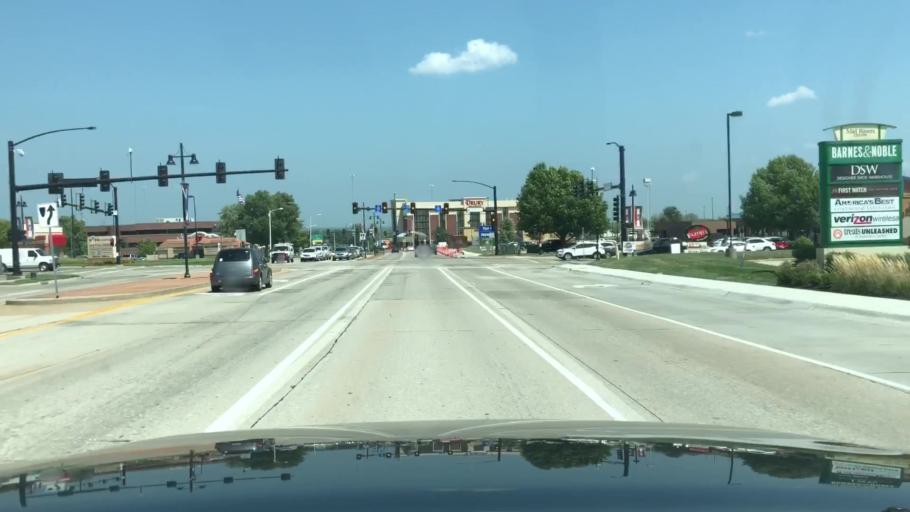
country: US
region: Missouri
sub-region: Saint Charles County
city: Saint Peters
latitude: 38.7955
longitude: -90.6218
